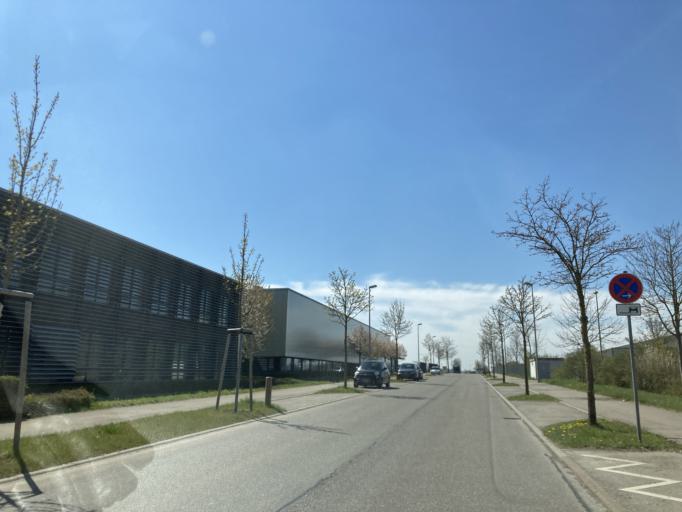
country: DE
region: Baden-Wuerttemberg
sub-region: Regierungsbezirk Stuttgart
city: Bondorf
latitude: 48.5015
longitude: 8.8217
